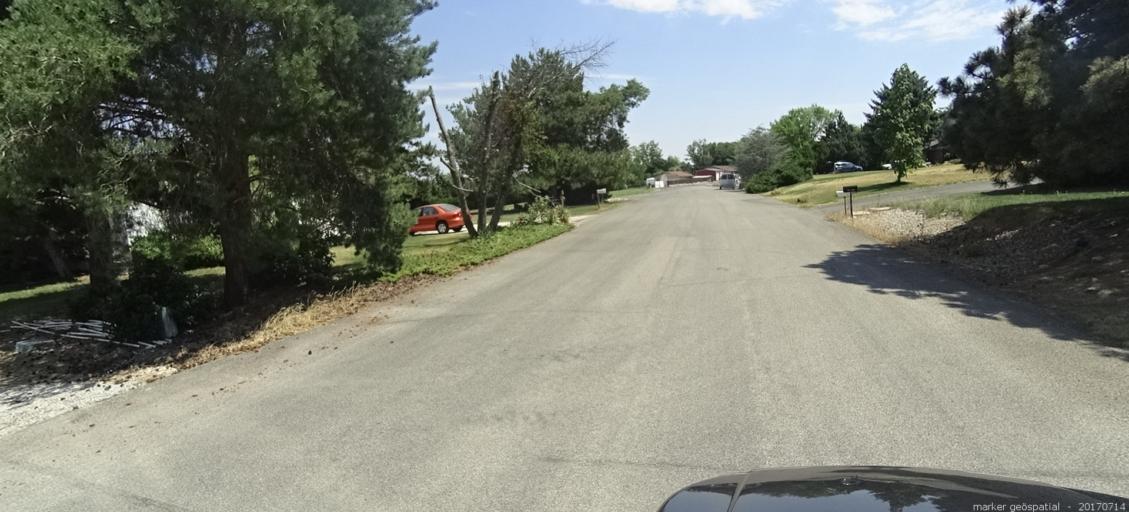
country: US
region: Idaho
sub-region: Ada County
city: Meridian
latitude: 43.5380
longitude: -116.3260
